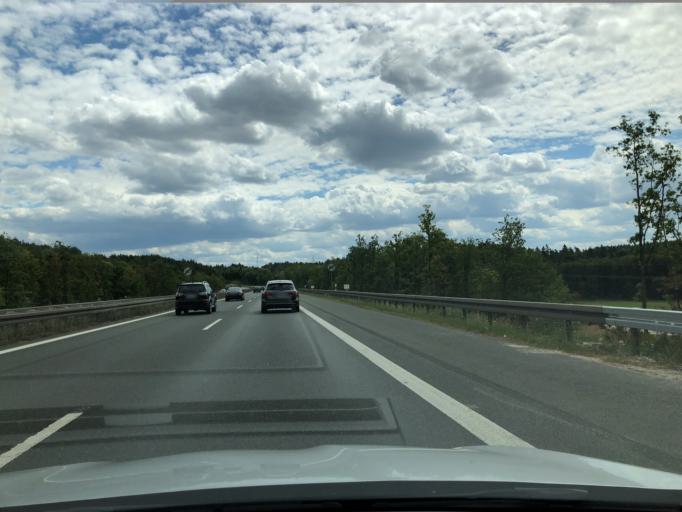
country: DE
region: Bavaria
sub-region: Regierungsbezirk Mittelfranken
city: Altdorf
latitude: 49.4036
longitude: 11.3681
